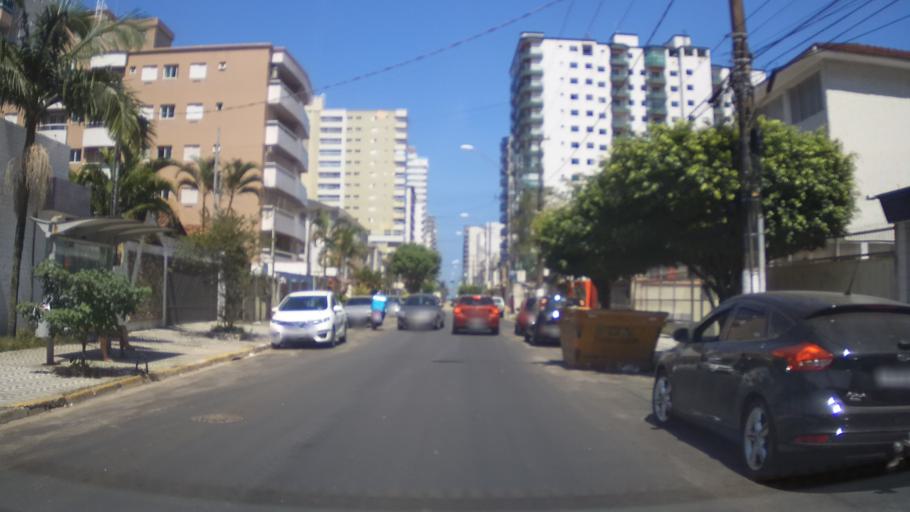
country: BR
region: Sao Paulo
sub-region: Praia Grande
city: Praia Grande
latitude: -24.0090
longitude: -46.4065
